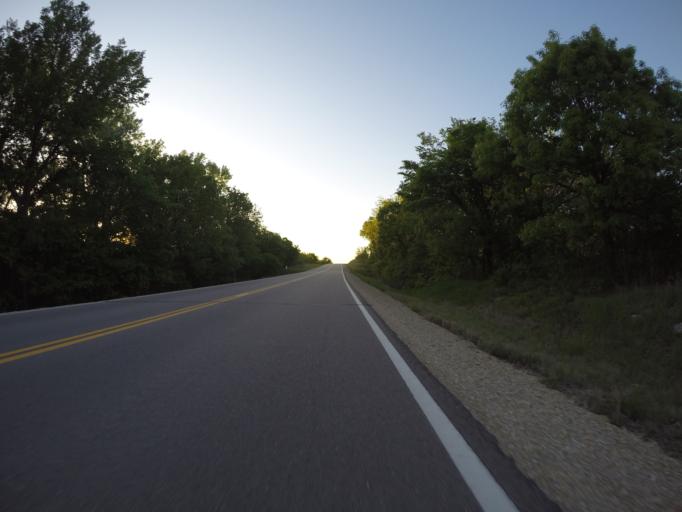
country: US
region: Kansas
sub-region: Riley County
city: Fort Riley North
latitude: 39.2477
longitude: -96.7688
